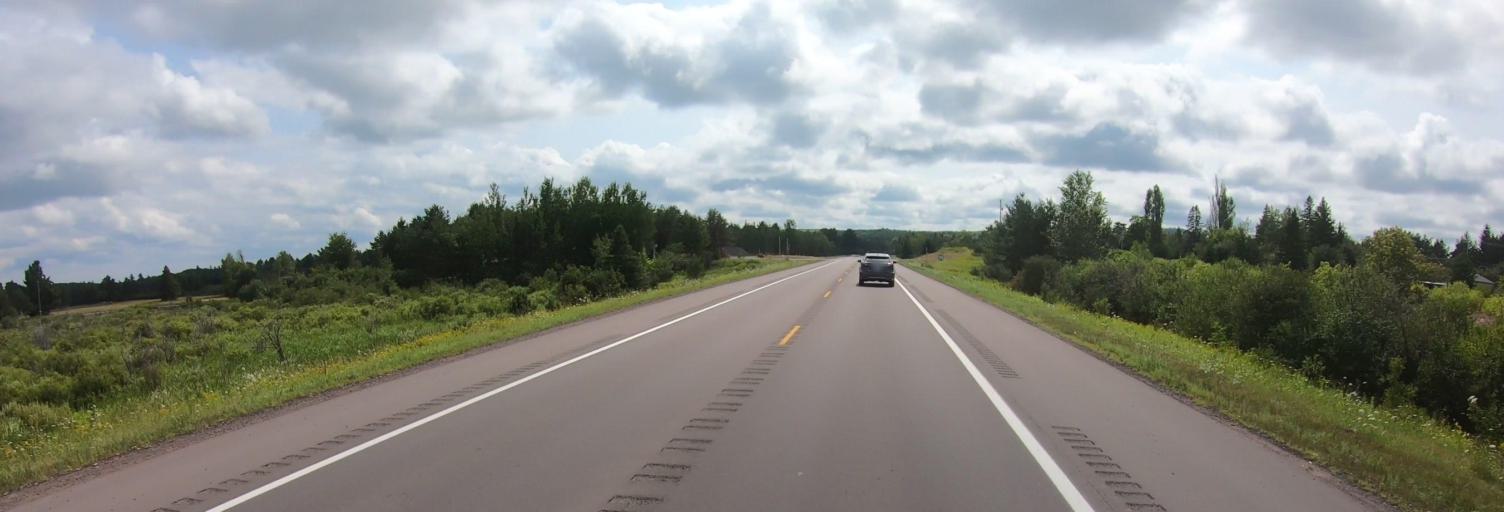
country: US
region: Michigan
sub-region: Houghton County
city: Hancock
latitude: 47.0923
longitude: -88.6242
